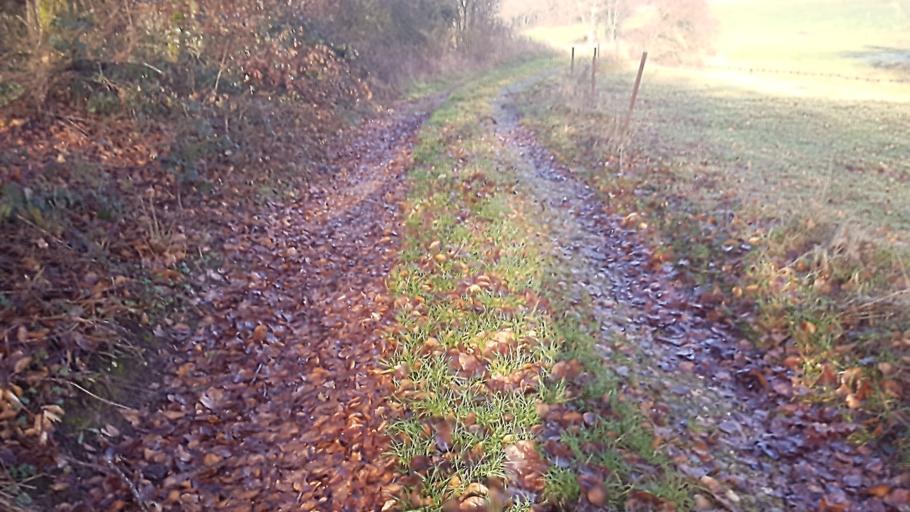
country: FR
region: Champagne-Ardenne
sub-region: Departement des Ardennes
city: Vireux-Molhain
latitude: 50.0750
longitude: 4.6190
